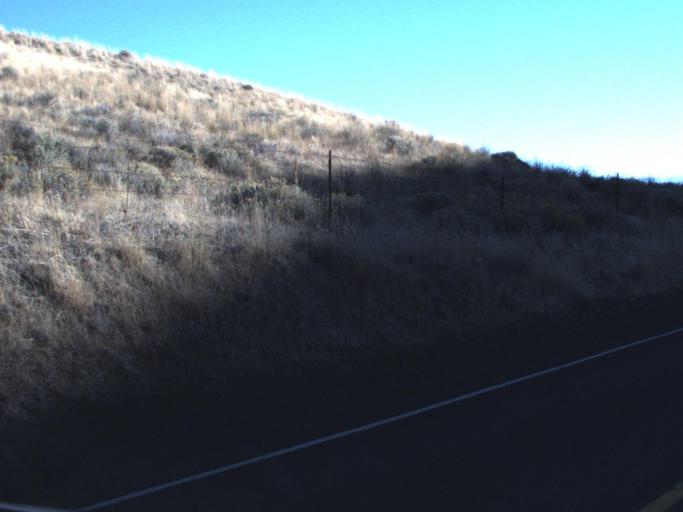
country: US
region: Washington
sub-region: Walla Walla County
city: Waitsburg
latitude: 46.6212
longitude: -118.2323
